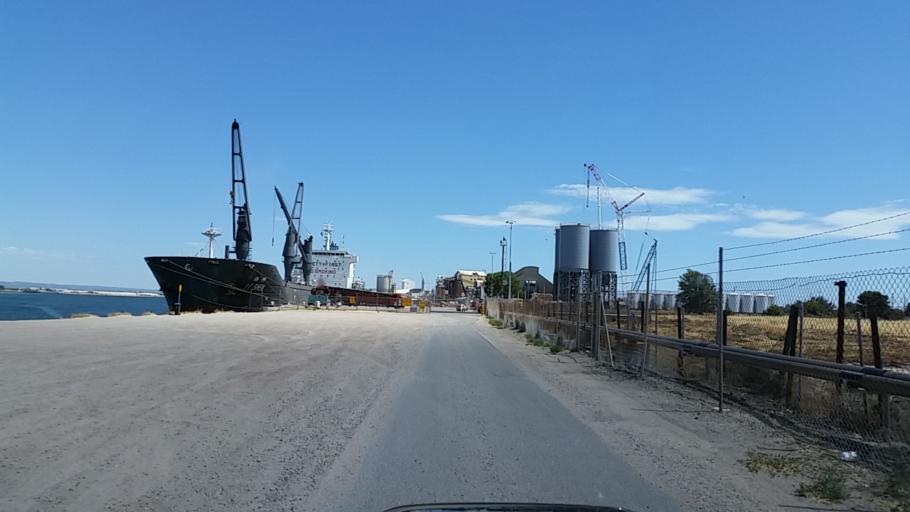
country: AU
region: South Australia
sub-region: Port Adelaide Enfield
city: Birkenhead
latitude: -34.7917
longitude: 138.5103
